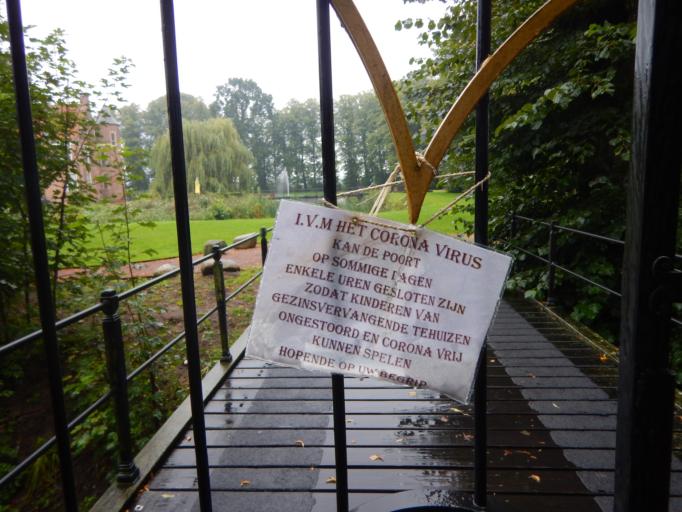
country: NL
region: Groningen
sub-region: Gemeente Vlagtwedde
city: Vlagtwedde
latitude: 53.0680
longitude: 7.0720
